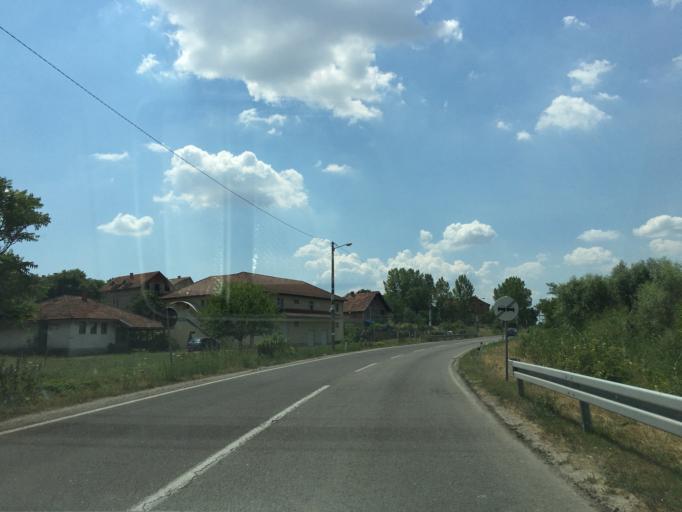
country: RS
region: Central Serbia
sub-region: Belgrade
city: Mladenovac
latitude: 44.4741
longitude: 20.6655
